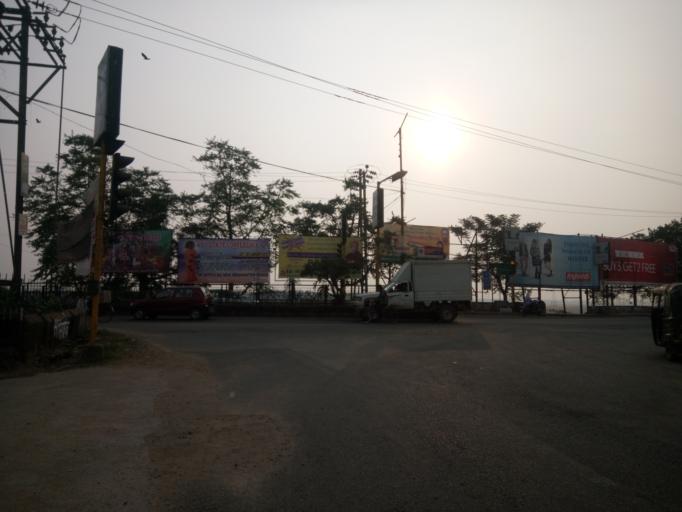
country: IN
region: Odisha
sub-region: Cuttack
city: Cuttack
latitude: 20.4548
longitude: 85.8782
